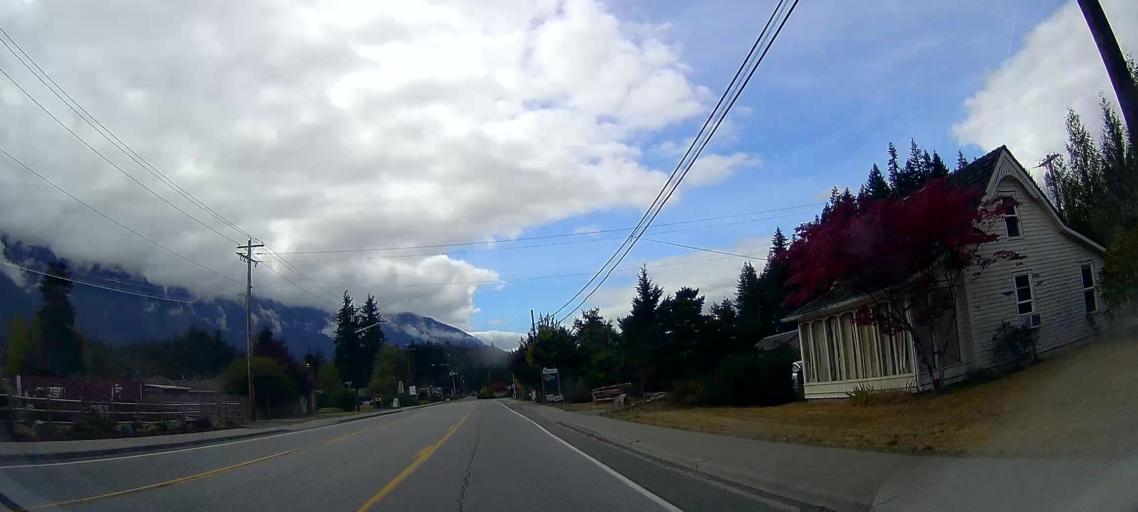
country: US
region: Washington
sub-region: Snohomish County
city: Darrington
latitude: 48.2553
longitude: -121.6068
